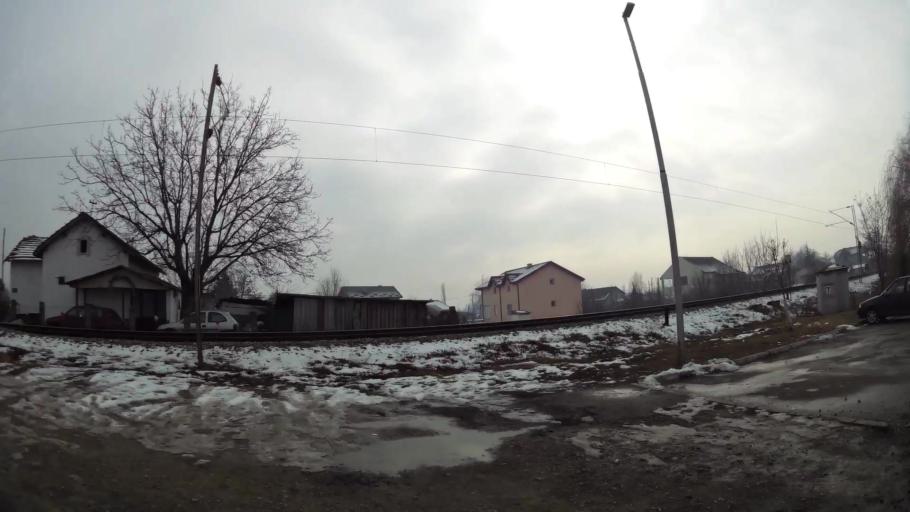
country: MK
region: Ilinden
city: Ilinden
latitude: 41.9952
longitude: 21.5564
